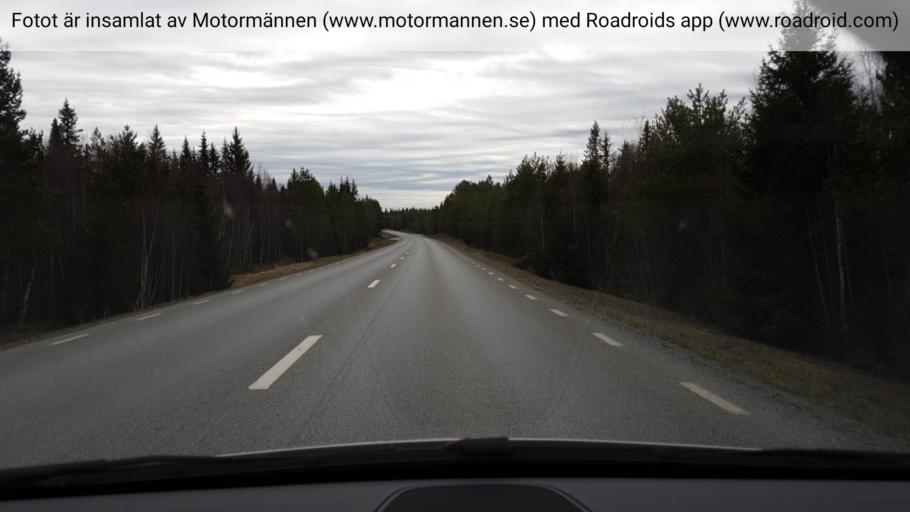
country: SE
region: Jaemtland
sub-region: Krokoms Kommun
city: Valla
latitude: 63.2949
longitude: 13.9269
